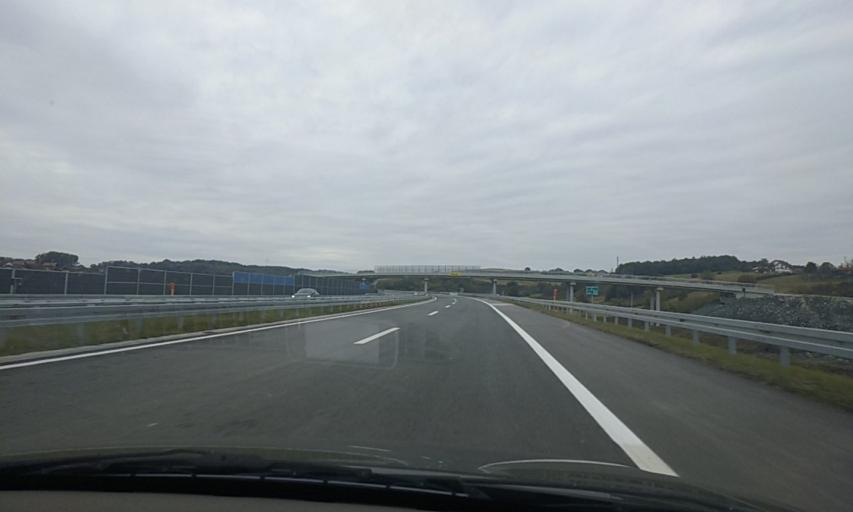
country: BA
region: Republika Srpska
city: Prnjavor
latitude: 44.8840
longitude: 17.5422
